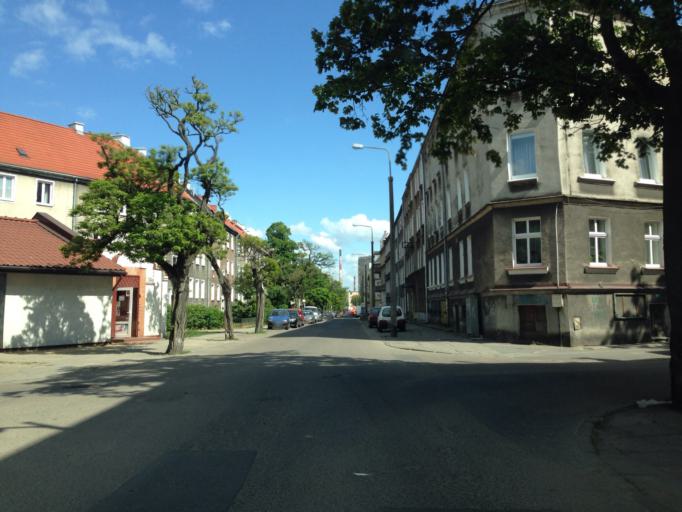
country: PL
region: Pomeranian Voivodeship
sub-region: Gdansk
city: Gdansk
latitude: 54.3840
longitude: 18.6095
